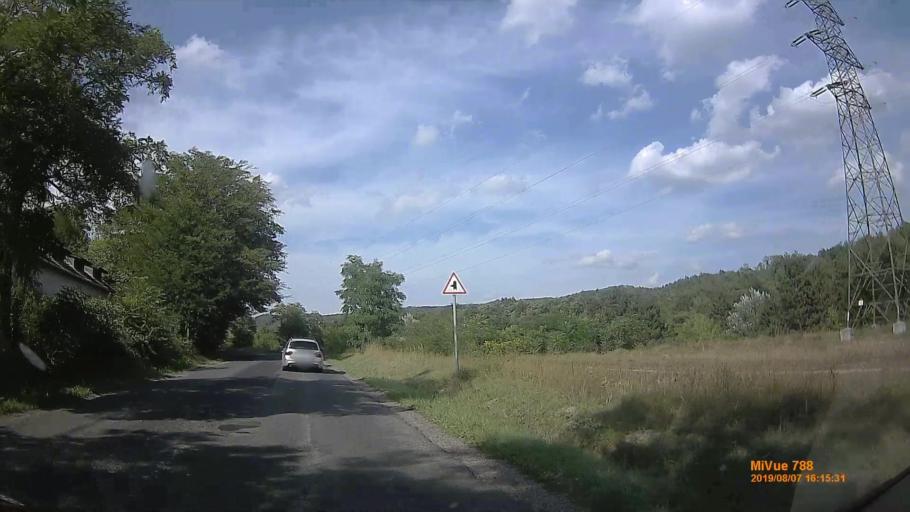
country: HU
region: Zala
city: Gyenesdias
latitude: 46.8016
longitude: 17.2701
